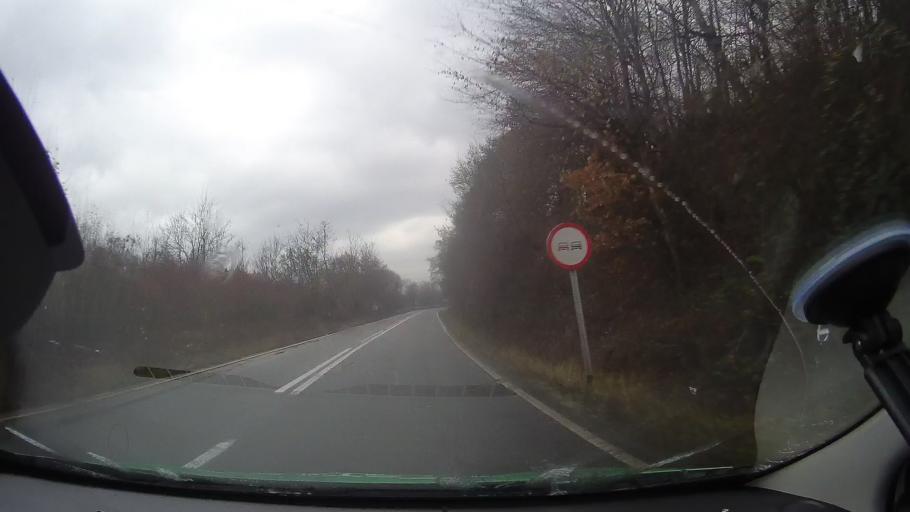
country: RO
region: Arad
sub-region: Comuna Almas
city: Almas
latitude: 46.3003
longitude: 22.2022
